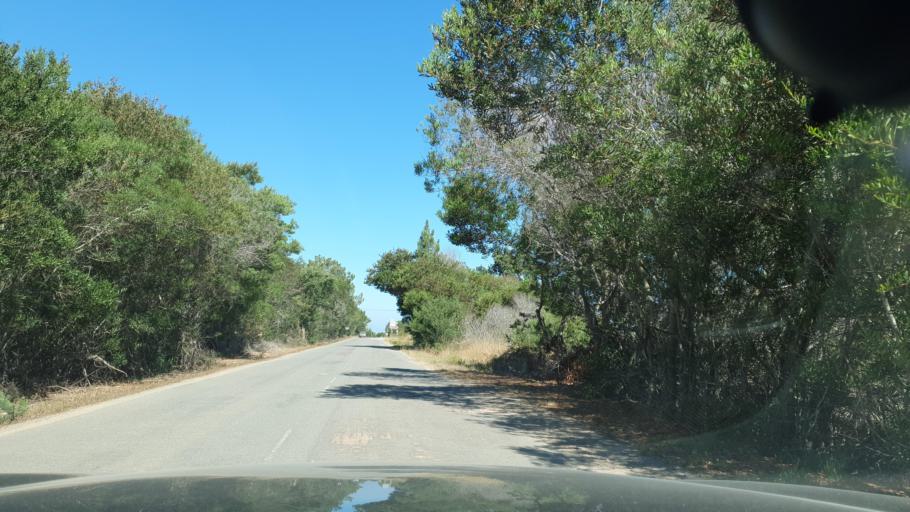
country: PT
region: Beja
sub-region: Odemira
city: Sao Teotonio
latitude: 37.5002
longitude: -8.6857
